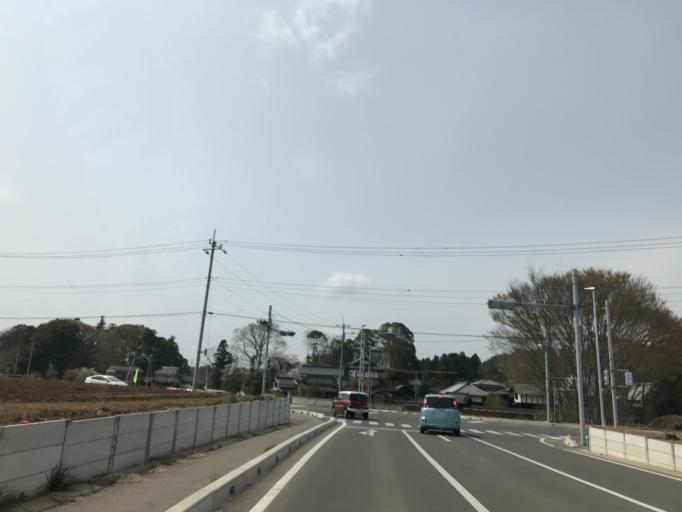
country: JP
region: Ibaraki
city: Naka
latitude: 36.0603
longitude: 140.0868
